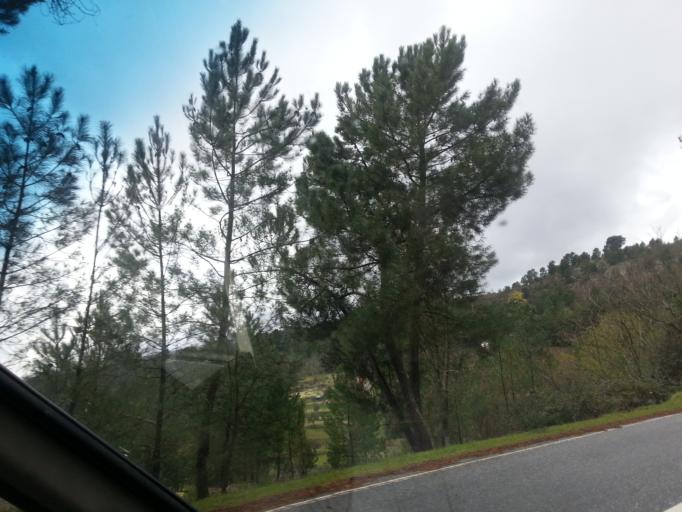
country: PT
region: Guarda
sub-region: Fornos de Algodres
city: Fornos de Algodres
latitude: 40.6086
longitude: -7.5751
